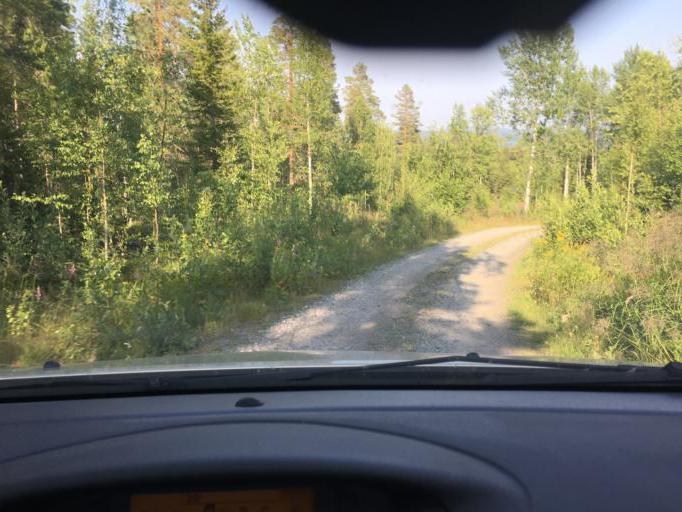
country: SE
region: Norrbotten
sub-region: Kalix Kommun
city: Toere
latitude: 65.8692
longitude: 22.6416
